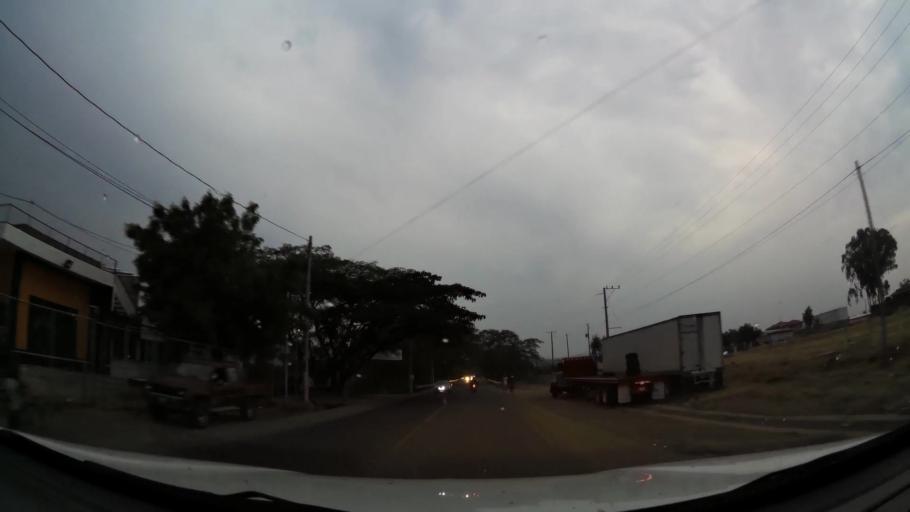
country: NI
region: Esteli
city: Esteli
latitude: 13.1050
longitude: -86.3548
